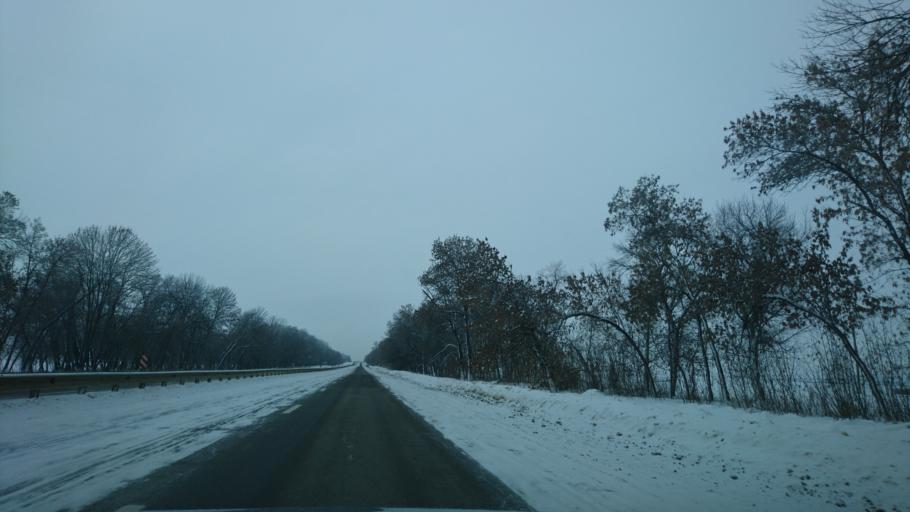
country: RU
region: Belgorod
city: Mayskiy
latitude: 50.4301
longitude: 36.3851
